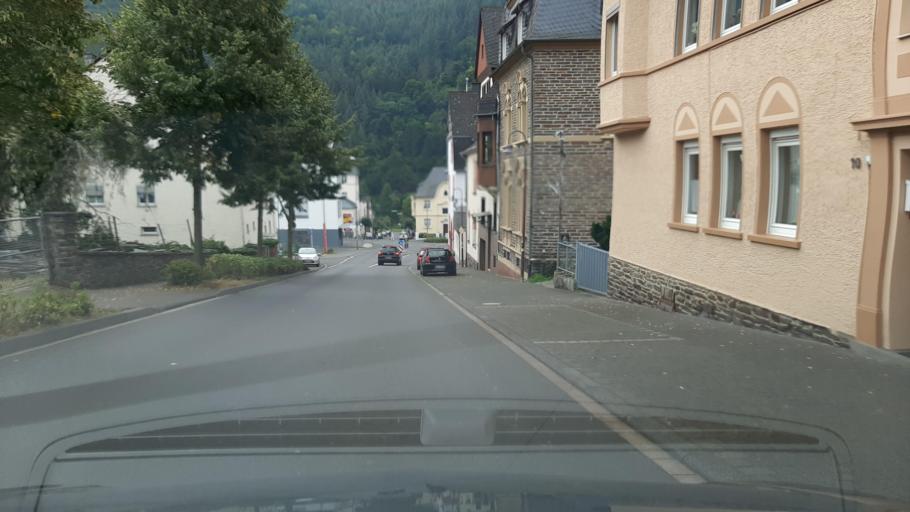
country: DE
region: Rheinland-Pfalz
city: Traben-Trarbach
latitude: 49.9523
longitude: 7.1200
